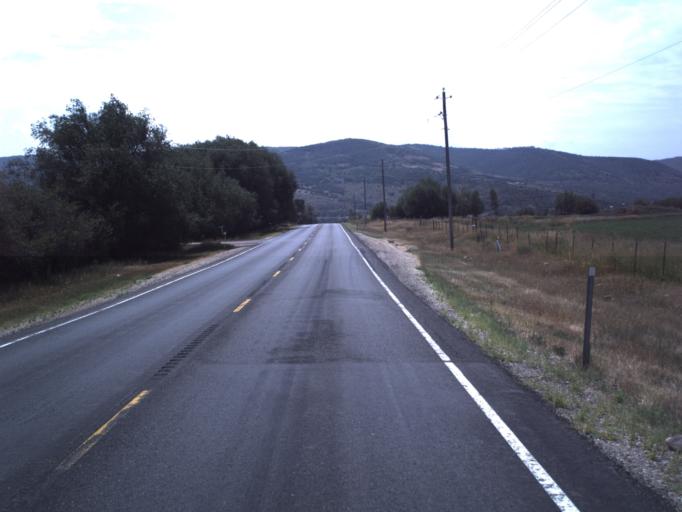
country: US
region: Utah
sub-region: Summit County
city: Francis
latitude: 40.5917
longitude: -111.2423
